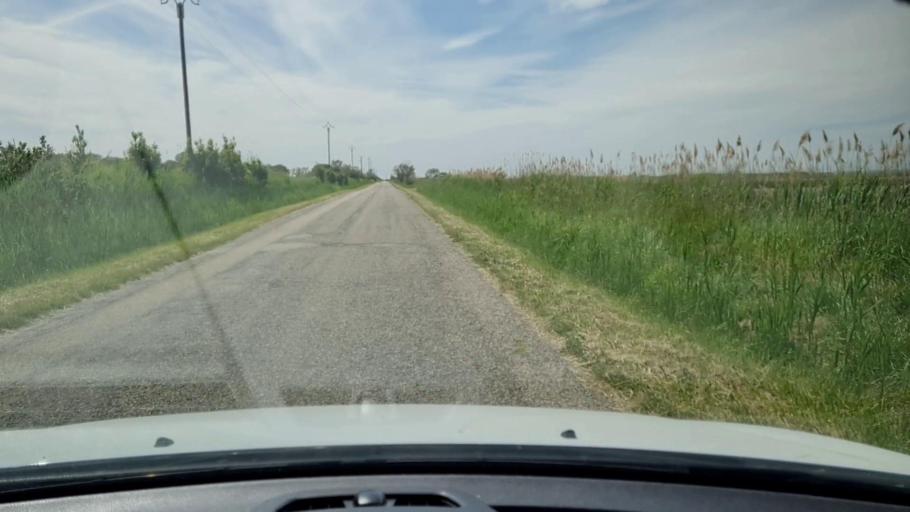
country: FR
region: Languedoc-Roussillon
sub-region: Departement du Gard
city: Saint-Gilles
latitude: 43.5895
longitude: 4.4374
